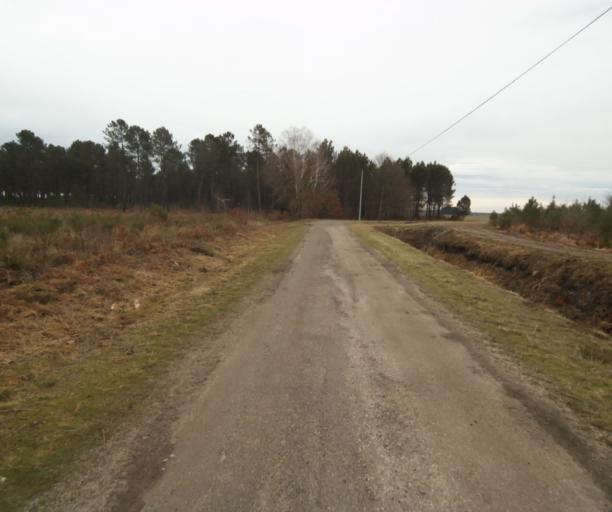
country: FR
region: Aquitaine
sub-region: Departement des Landes
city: Gabarret
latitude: 44.0347
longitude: -0.0288
